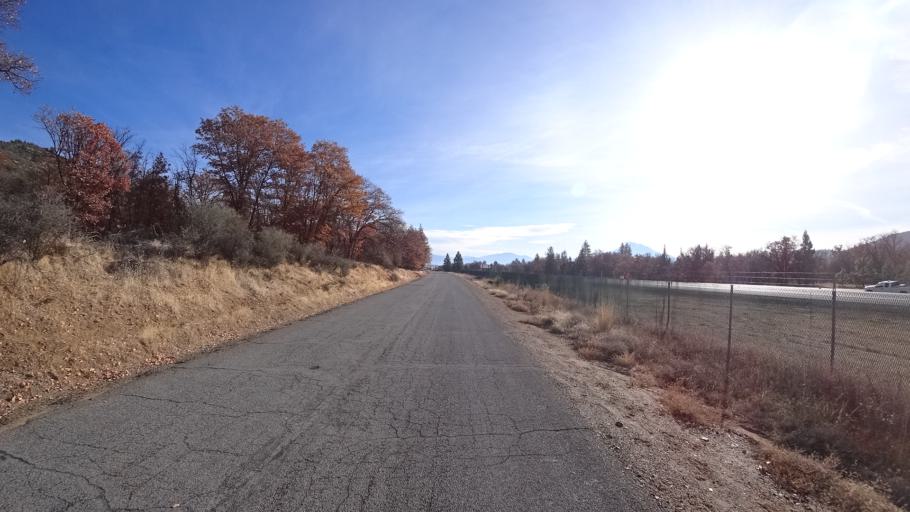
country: US
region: California
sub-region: Siskiyou County
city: Yreka
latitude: 41.6619
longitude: -122.5958
